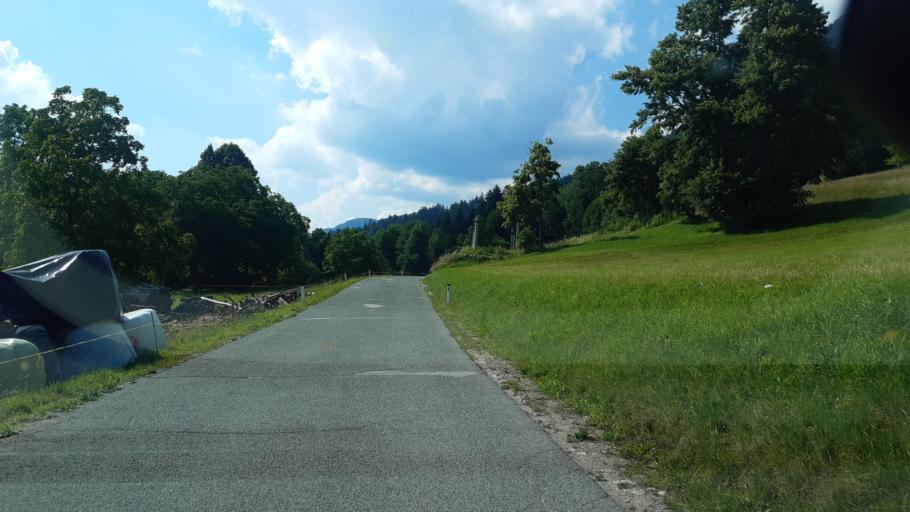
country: SI
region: Trzic
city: Bistrica pri Trzicu
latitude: 46.3651
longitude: 14.2326
